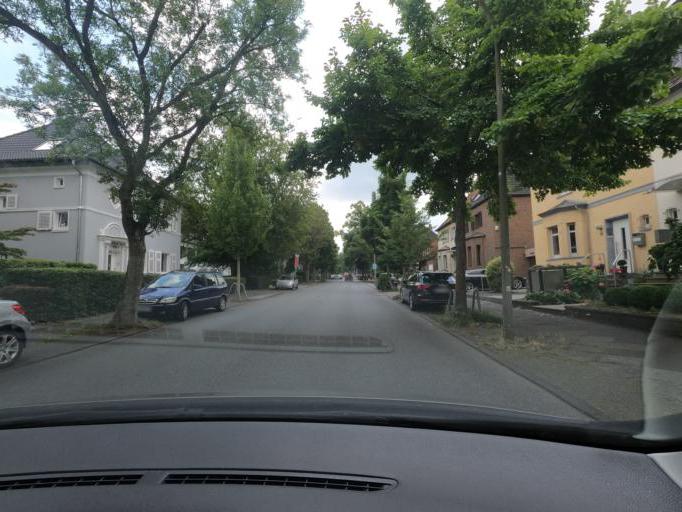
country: DE
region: North Rhine-Westphalia
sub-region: Regierungsbezirk Arnsberg
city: Dortmund
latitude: 51.5058
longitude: 7.5078
